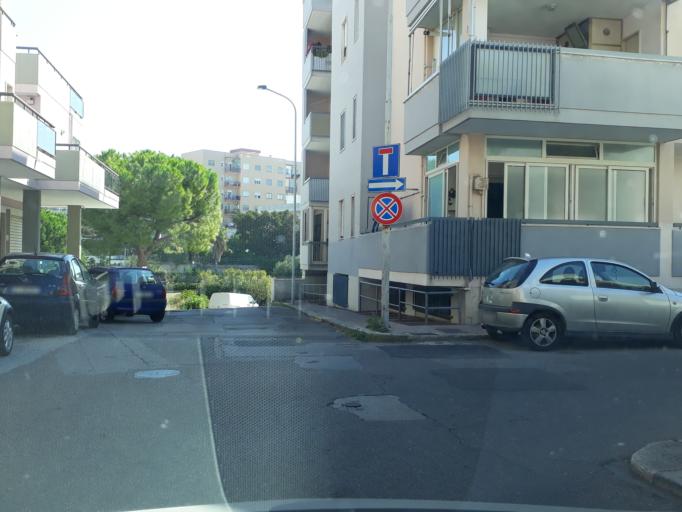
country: IT
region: Apulia
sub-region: Provincia di Bari
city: Monopoli
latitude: 40.9486
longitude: 17.2942
